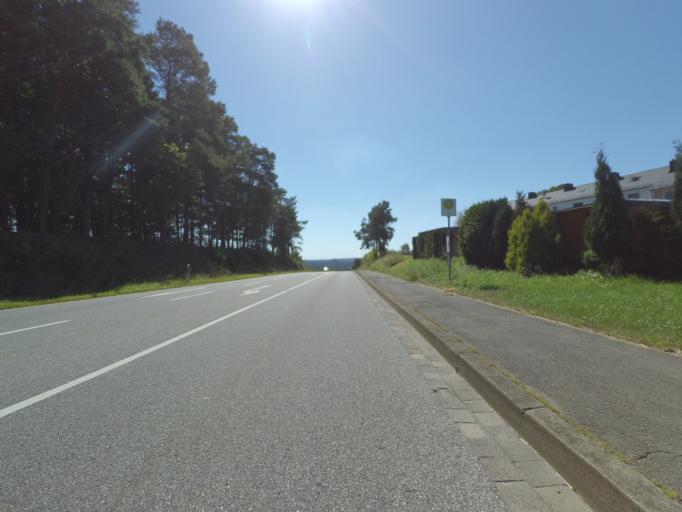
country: DE
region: Rheinland-Pfalz
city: Ulmen
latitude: 50.2112
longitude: 6.9701
